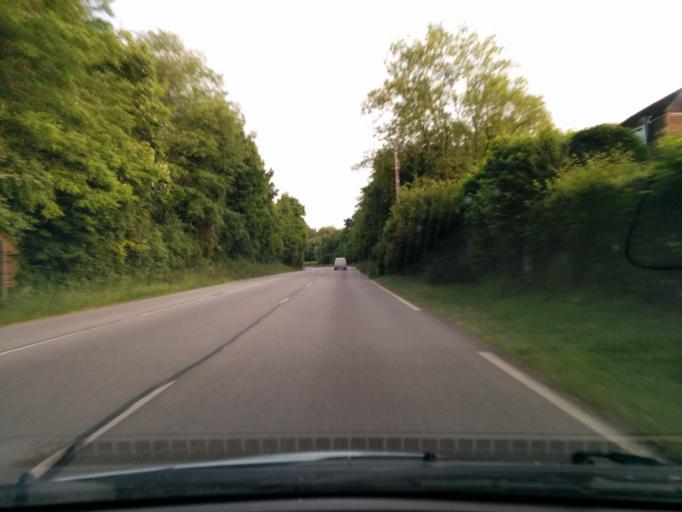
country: FR
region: Haute-Normandie
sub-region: Departement de l'Eure
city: Vernon
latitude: 49.0780
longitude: 1.4616
